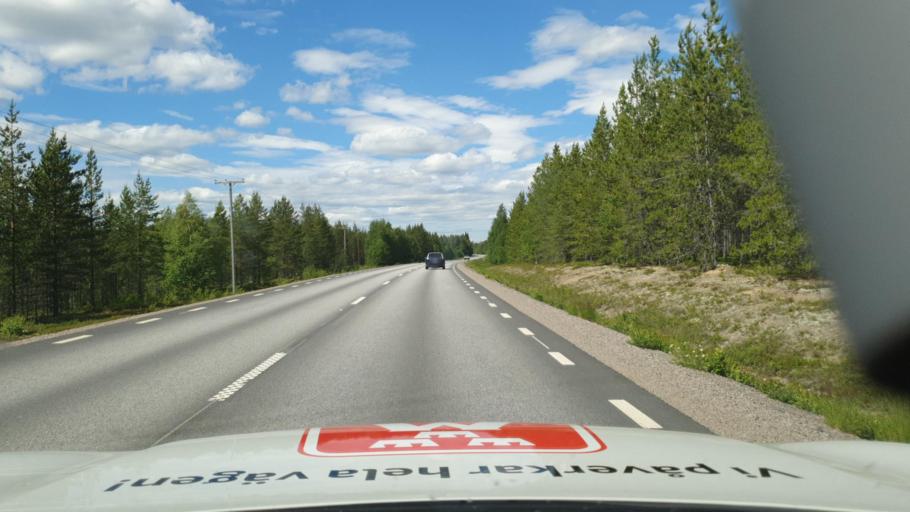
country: SE
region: Vaesterbotten
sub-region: Skelleftea Kommun
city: Langsele
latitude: 65.0262
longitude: 20.1156
